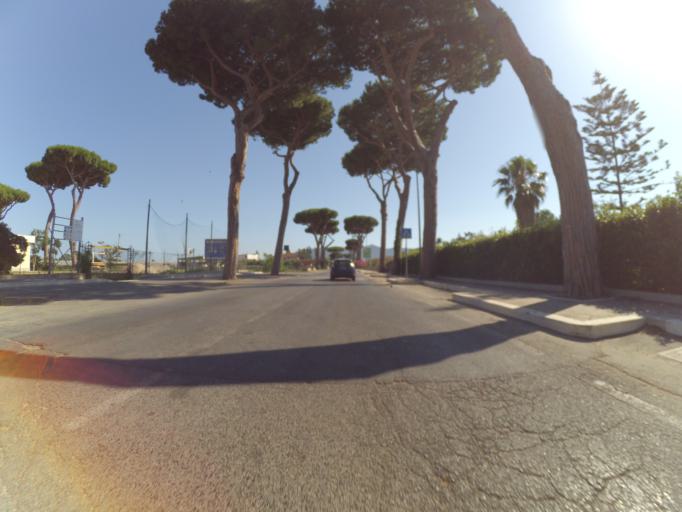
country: IT
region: Latium
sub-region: Provincia di Latina
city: San Felice Circeo
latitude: 41.2750
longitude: 13.1000
